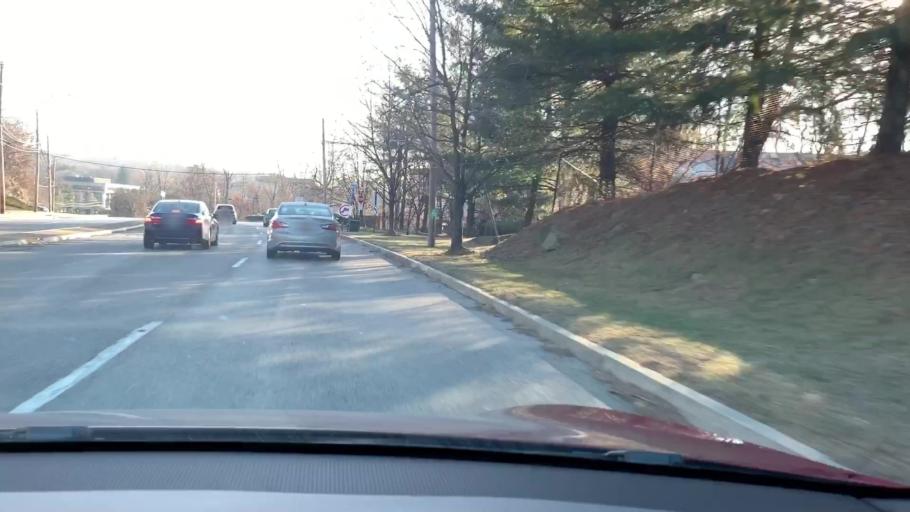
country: US
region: New York
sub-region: Westchester County
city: Tarrytown
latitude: 41.0633
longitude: -73.8455
